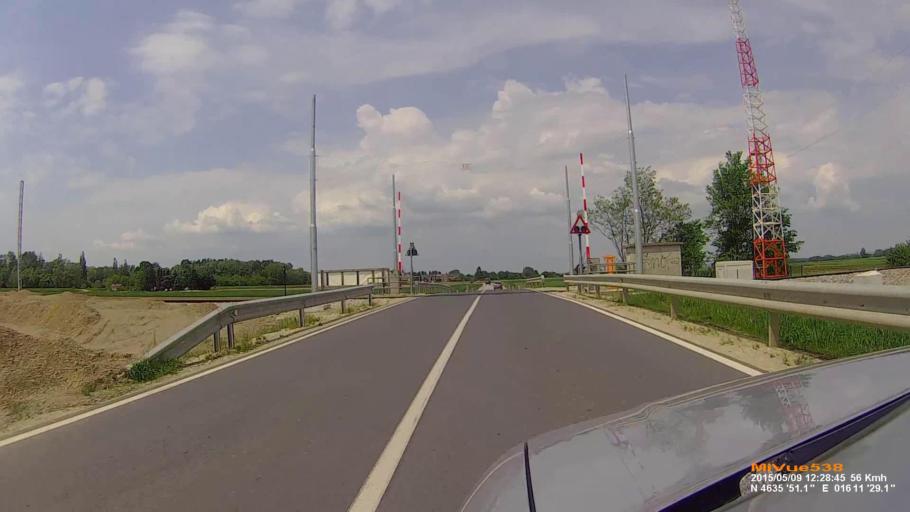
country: SI
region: Verzej
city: Verzej
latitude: 46.5975
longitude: 16.1916
